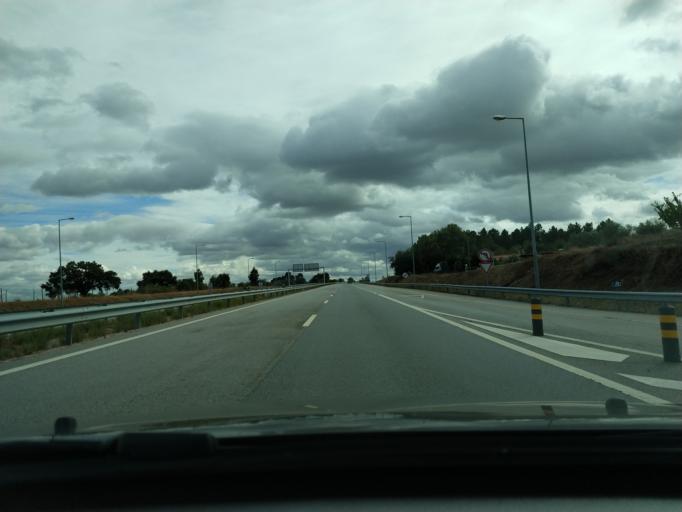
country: PT
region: Guarda
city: Alcains
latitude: 40.0263
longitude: -7.4670
